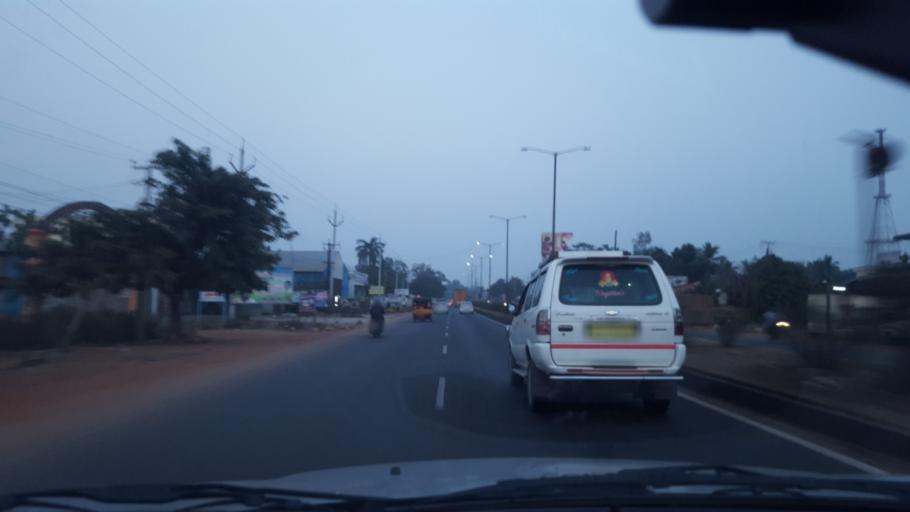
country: IN
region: Andhra Pradesh
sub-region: East Godavari
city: Rajahmundry
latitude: 17.0270
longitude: 81.8093
